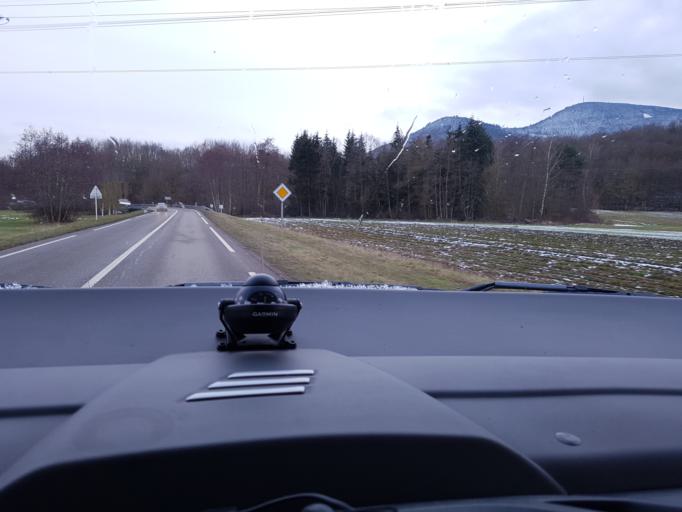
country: FR
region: Alsace
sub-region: Departement du Bas-Rhin
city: Ville
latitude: 48.3176
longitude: 7.3490
